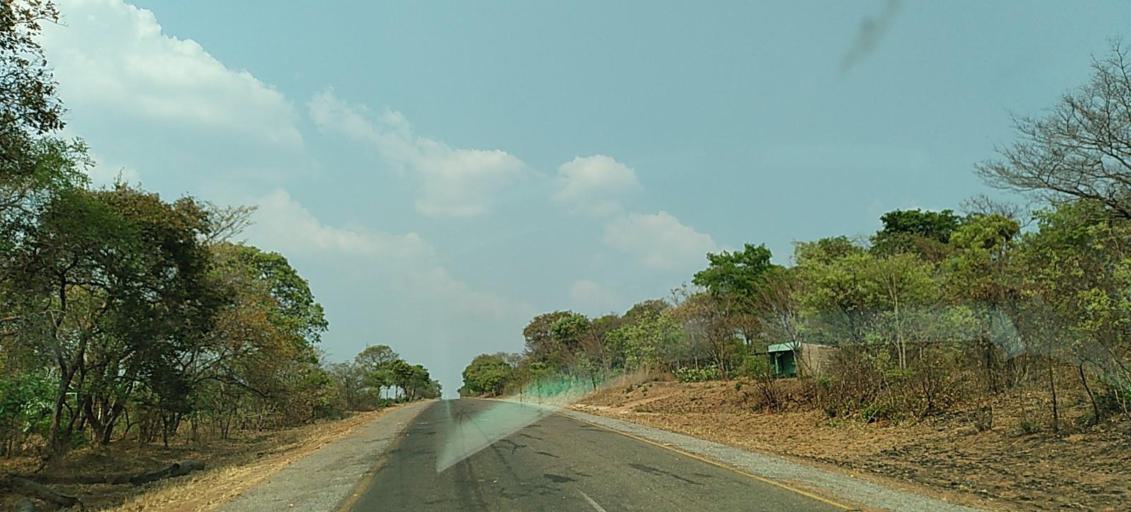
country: ZM
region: North-Western
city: Kabompo
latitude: -13.6187
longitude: 24.1262
